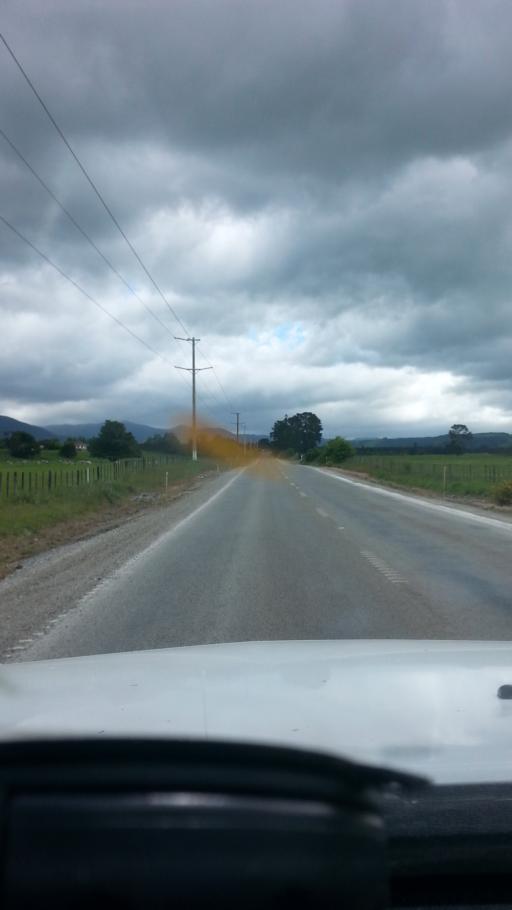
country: NZ
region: Wellington
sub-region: Masterton District
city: Masterton
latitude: -40.8318
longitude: 175.6275
